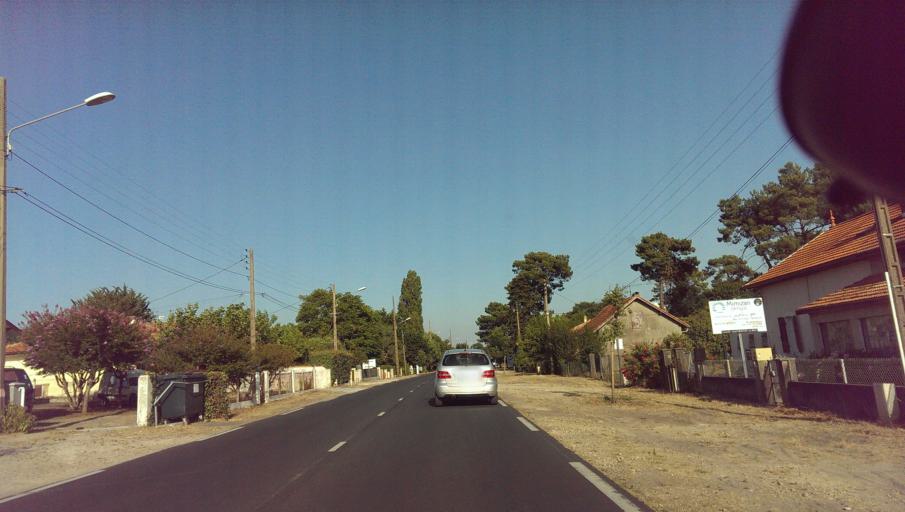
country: FR
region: Aquitaine
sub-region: Departement des Landes
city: Mimizan
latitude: 44.2106
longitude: -1.2558
